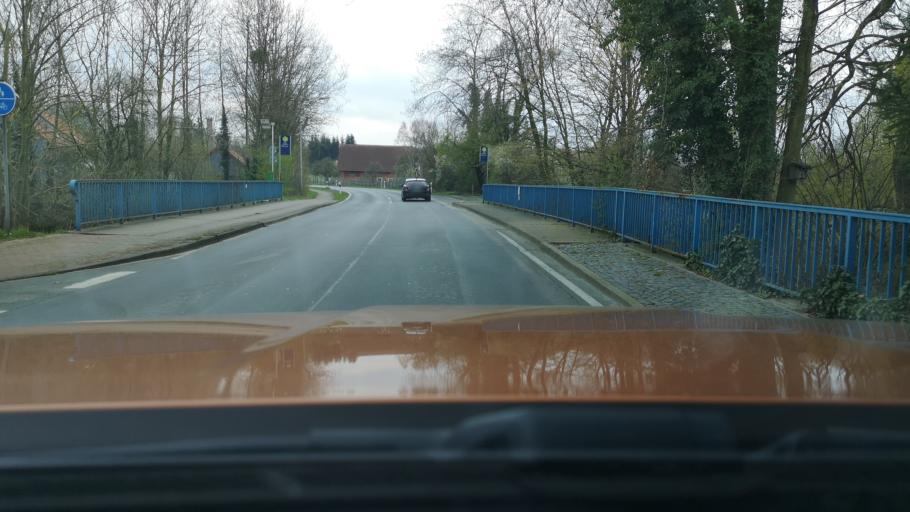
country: DE
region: Lower Saxony
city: Seggebruch
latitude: 52.2895
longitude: 9.0853
